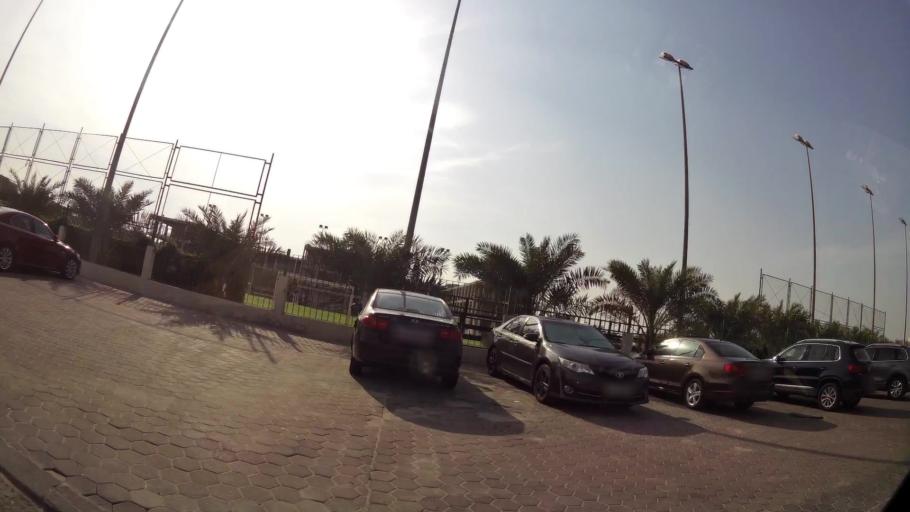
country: KW
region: Al Asimah
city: Ash Shamiyah
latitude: 29.3281
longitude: 47.9810
